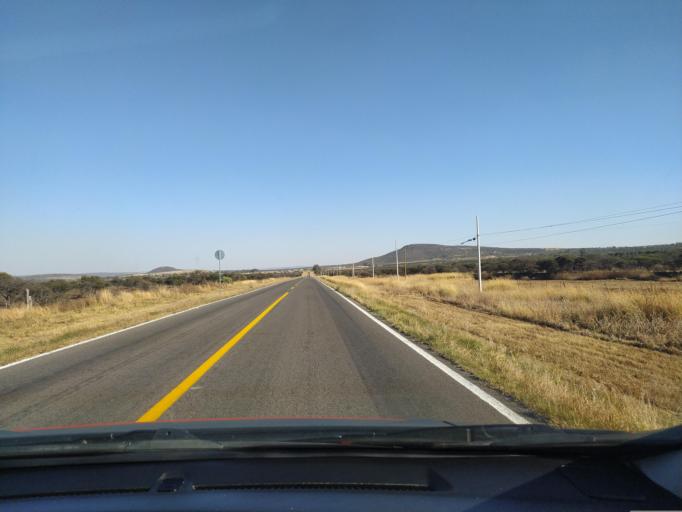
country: MX
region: Jalisco
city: San Miguel el Alto
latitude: 21.0169
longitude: -102.4903
